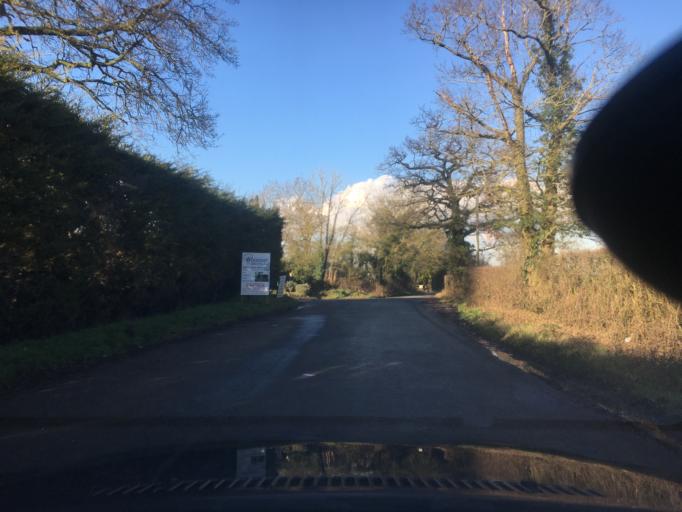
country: GB
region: England
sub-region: West Berkshire
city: Stratfield Mortimer
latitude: 51.3942
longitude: -1.0238
